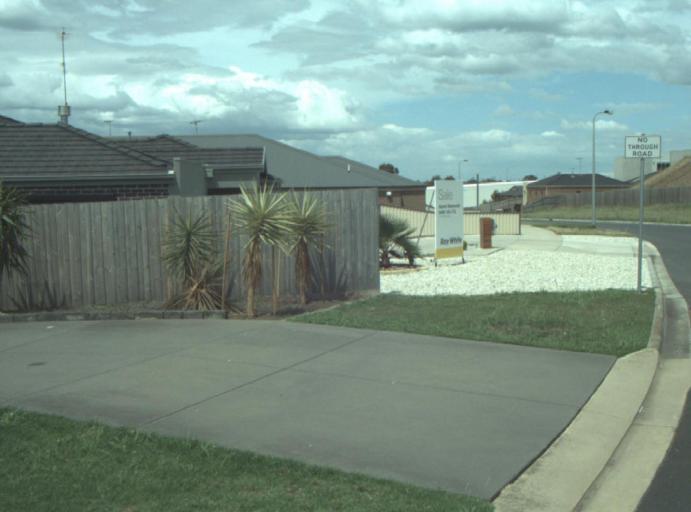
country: AU
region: Victoria
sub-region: Greater Geelong
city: Bell Park
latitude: -38.0952
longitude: 144.3416
